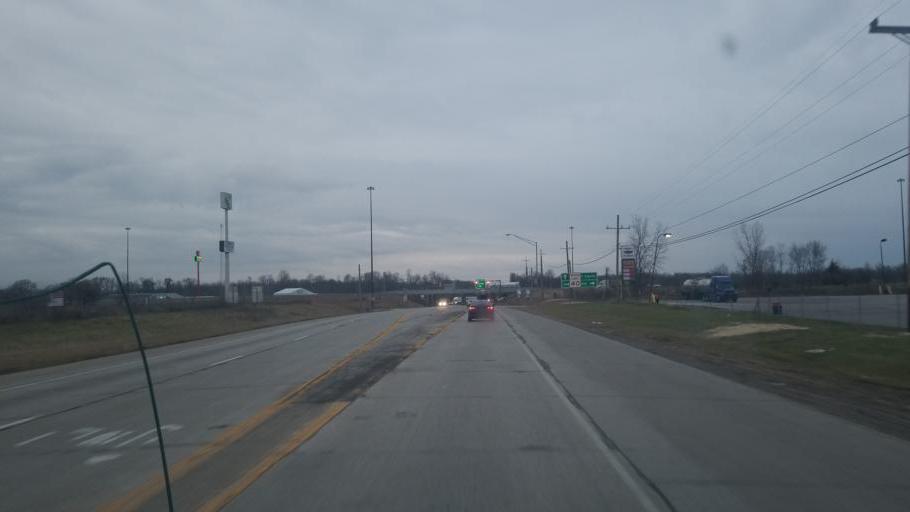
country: US
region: Indiana
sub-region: Clay County
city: Brazil
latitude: 39.4467
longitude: -87.1263
